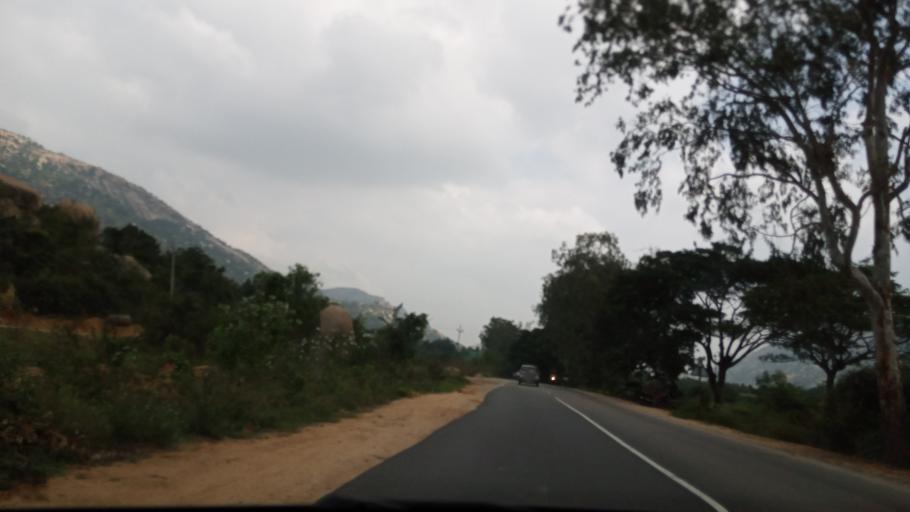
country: IN
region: Andhra Pradesh
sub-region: Chittoor
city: Madanapalle
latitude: 13.6368
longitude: 78.5792
